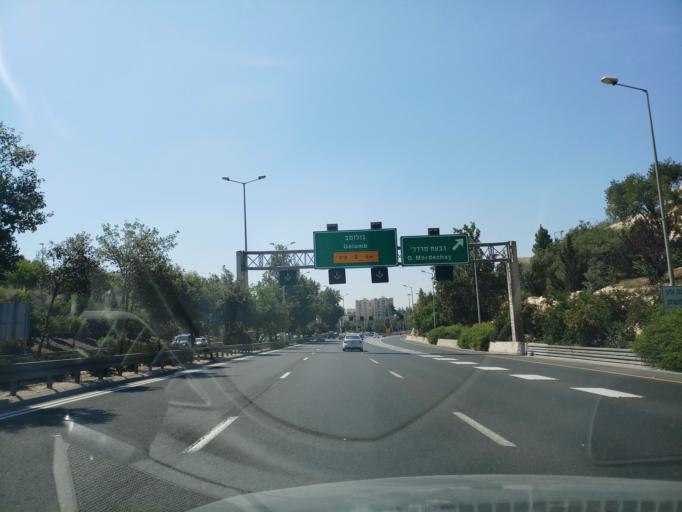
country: IL
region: Jerusalem
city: Jerusalem
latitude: 31.7714
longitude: 35.1946
